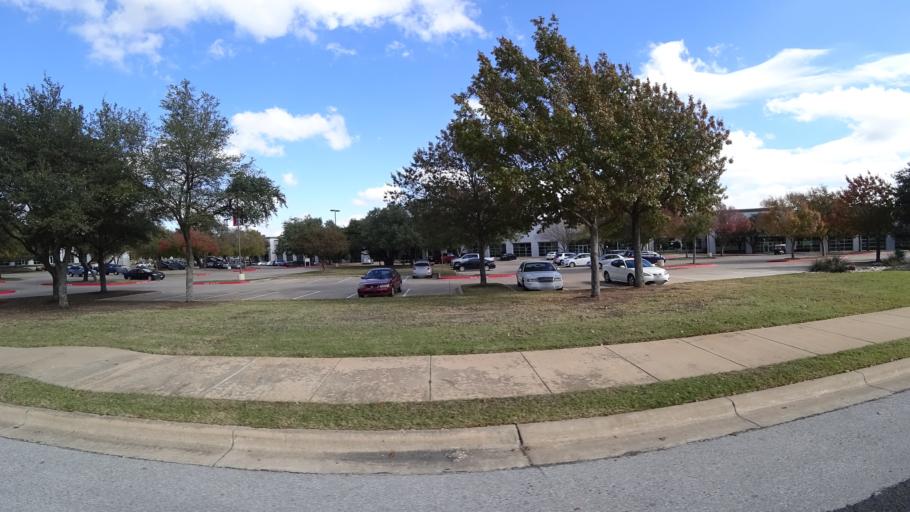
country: US
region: Texas
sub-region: Williamson County
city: Jollyville
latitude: 30.4317
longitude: -97.7315
